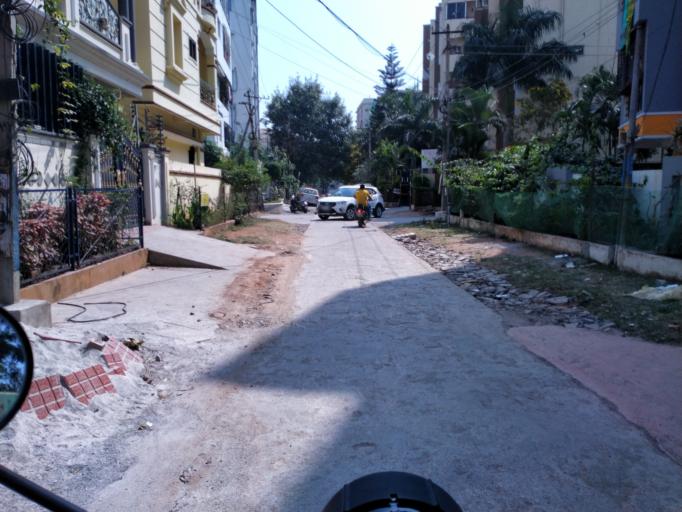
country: IN
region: Telangana
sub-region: Rangareddi
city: Secunderabad
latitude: 17.4960
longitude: 78.5459
